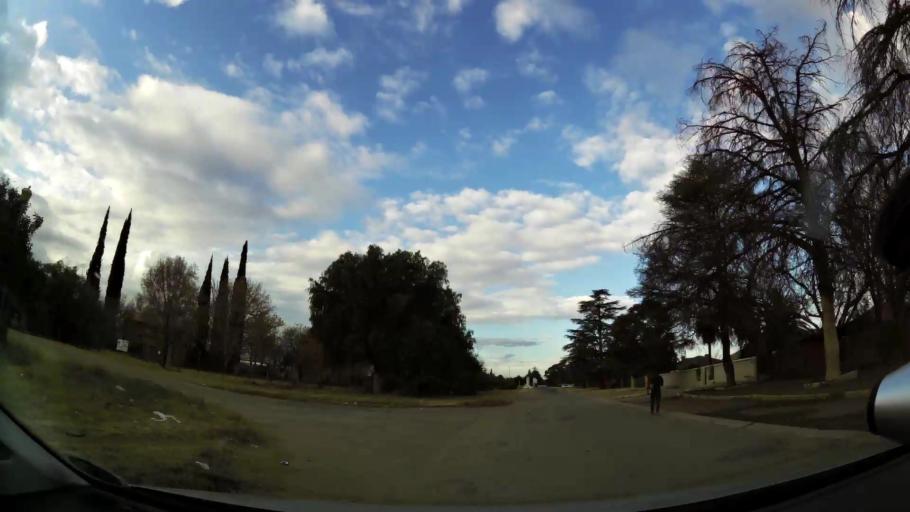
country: ZA
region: Orange Free State
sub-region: Lejweleputswa District Municipality
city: Welkom
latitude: -27.9917
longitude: 26.7106
